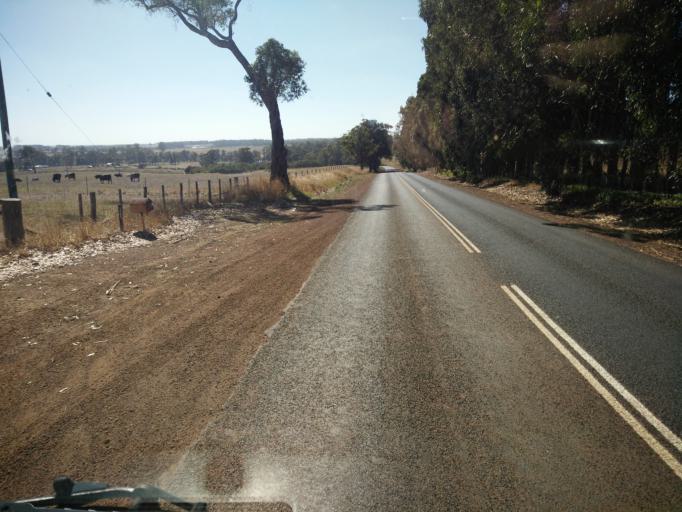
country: AU
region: Western Australia
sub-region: Manjimup
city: Manjimup
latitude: -34.2235
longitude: 115.9920
